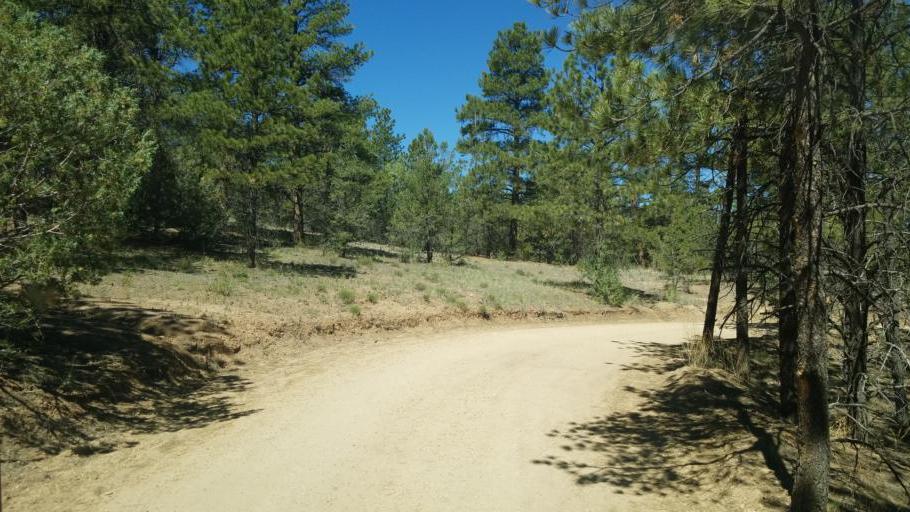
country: US
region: Colorado
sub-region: Custer County
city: Westcliffe
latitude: 38.2529
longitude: -105.5618
